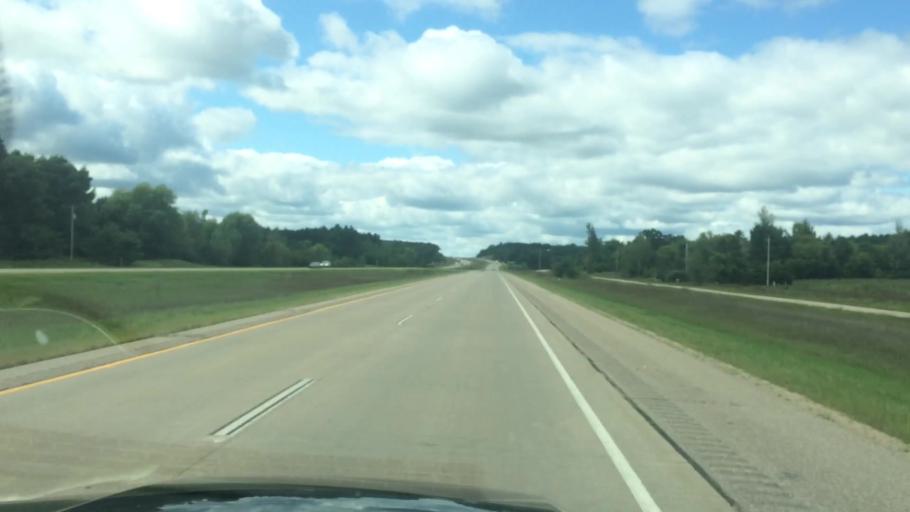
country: US
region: Wisconsin
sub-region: Waupaca County
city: King
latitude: 44.3782
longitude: -89.1685
